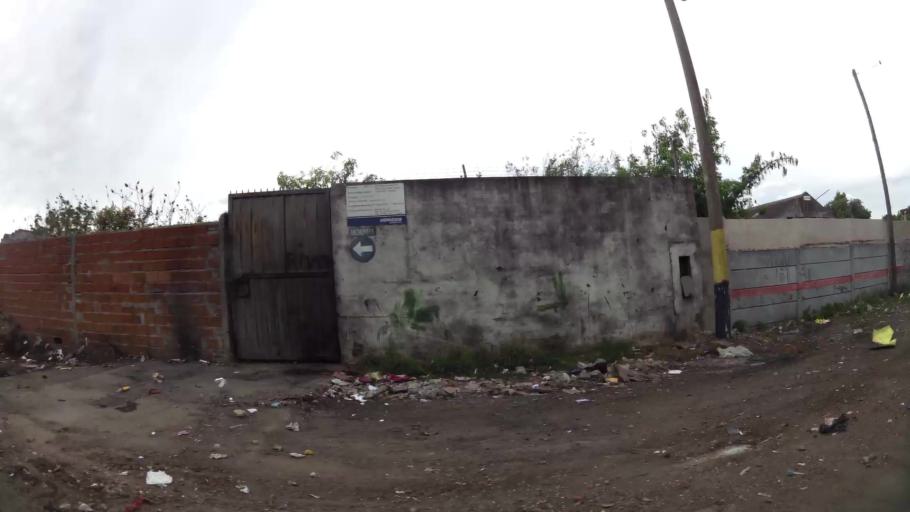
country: AR
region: Santa Fe
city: Gobernador Galvez
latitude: -32.9985
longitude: -60.6740
